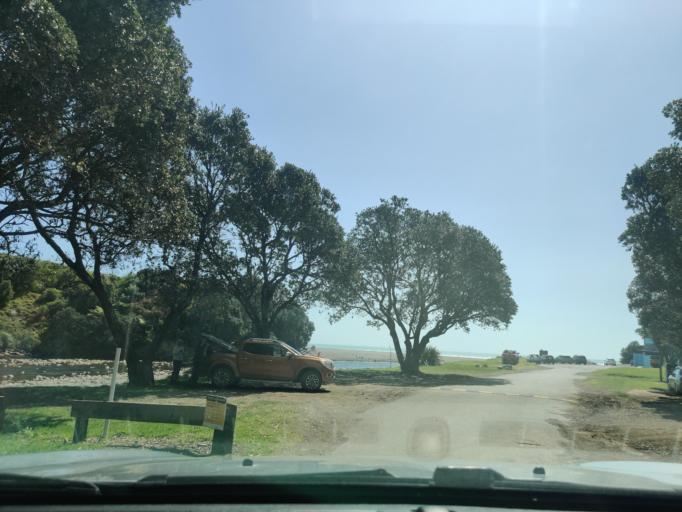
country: NZ
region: Taranaki
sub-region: New Plymouth District
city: New Plymouth
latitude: -39.1114
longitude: 173.9576
